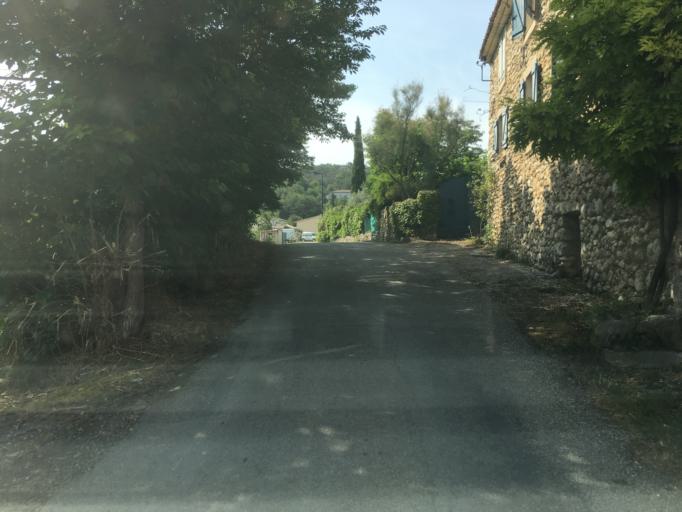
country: FR
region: Provence-Alpes-Cote d'Azur
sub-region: Departement des Alpes-de-Haute-Provence
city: Mallemoisson
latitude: 43.9406
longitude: 6.1699
